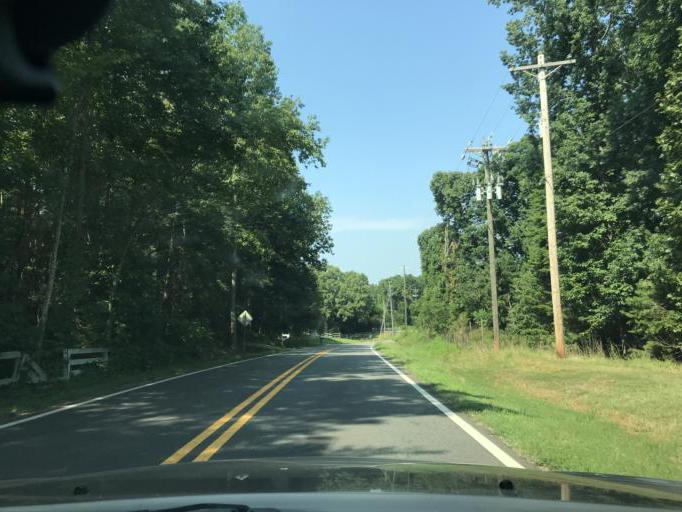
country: US
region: Georgia
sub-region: Hall County
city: Flowery Branch
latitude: 34.2323
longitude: -83.9989
